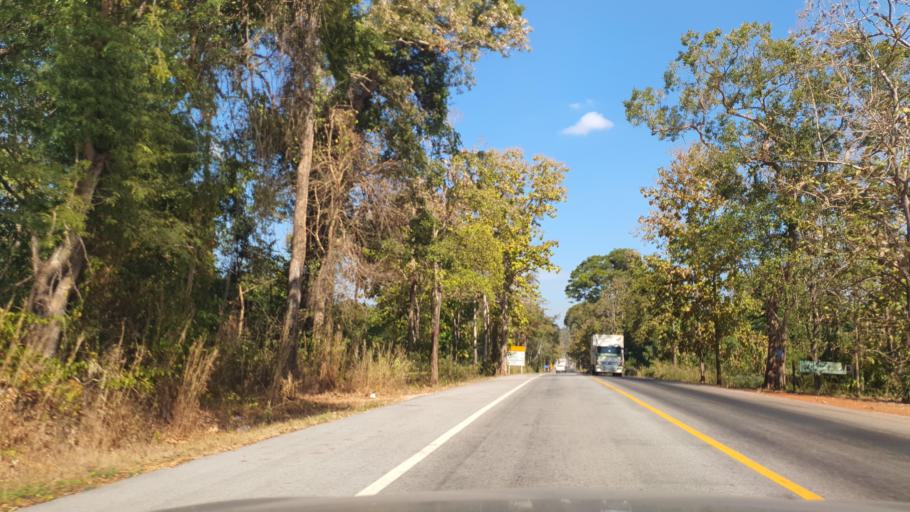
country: TH
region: Kalasin
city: Na Khu
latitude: 16.8508
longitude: 103.9277
